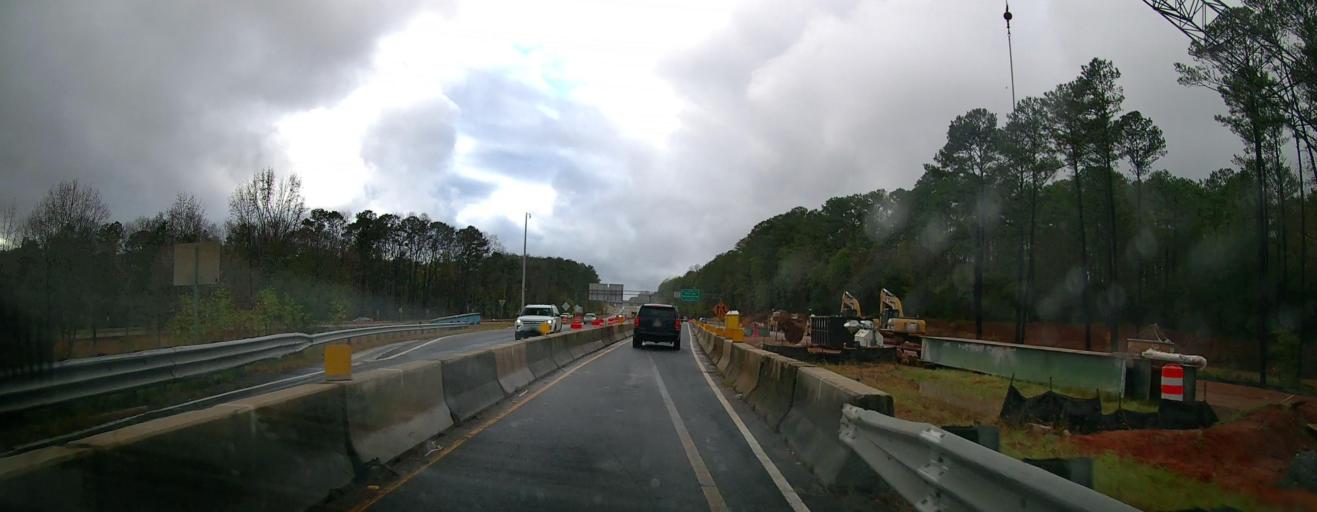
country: US
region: Georgia
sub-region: Clarke County
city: Athens
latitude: 33.9779
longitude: -83.3527
